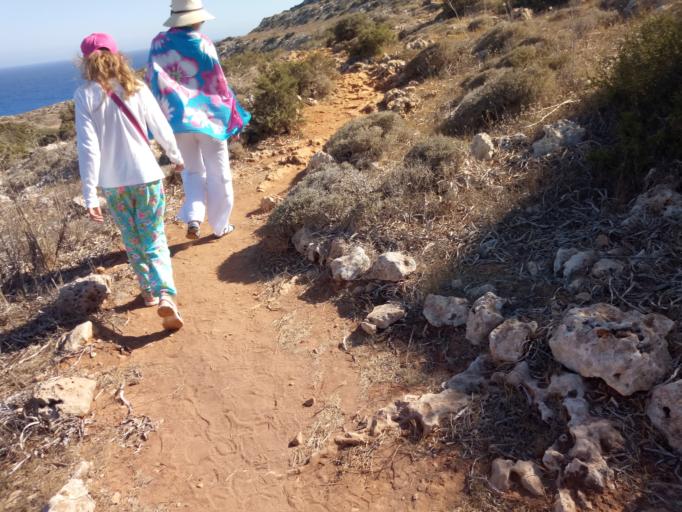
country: CY
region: Ammochostos
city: Protaras
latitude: 34.9685
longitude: 34.0720
